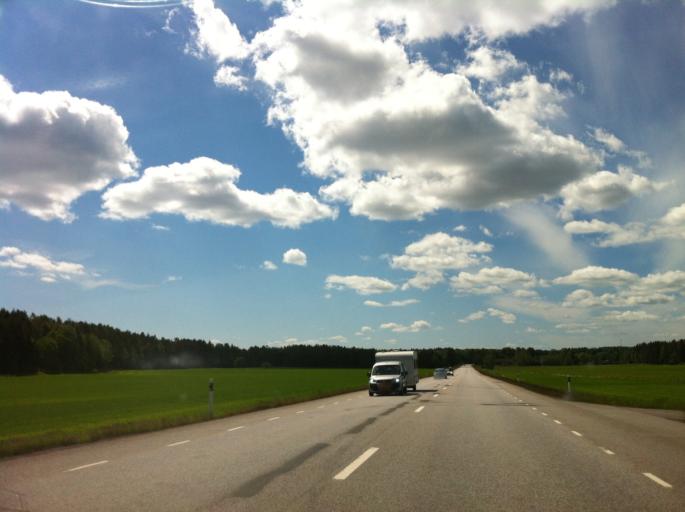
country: SE
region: Vaestra Goetaland
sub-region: Amals Kommun
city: Amal
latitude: 59.0125
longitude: 12.6914
